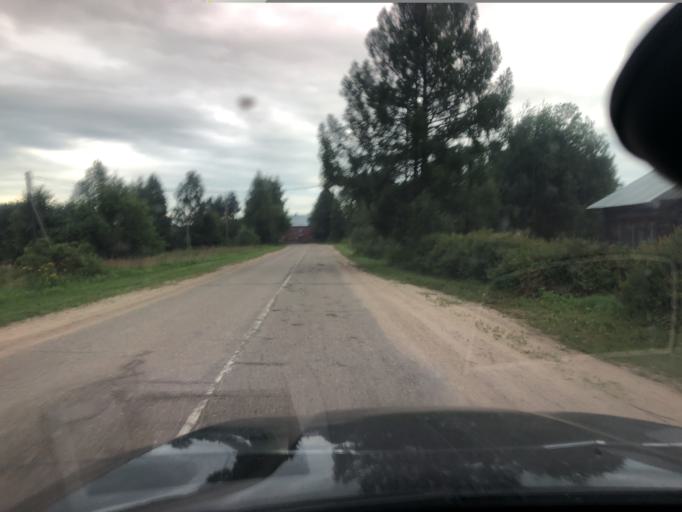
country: RU
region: Jaroslavl
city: Pereslavl'-Zalesskiy
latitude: 57.0305
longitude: 38.9138
